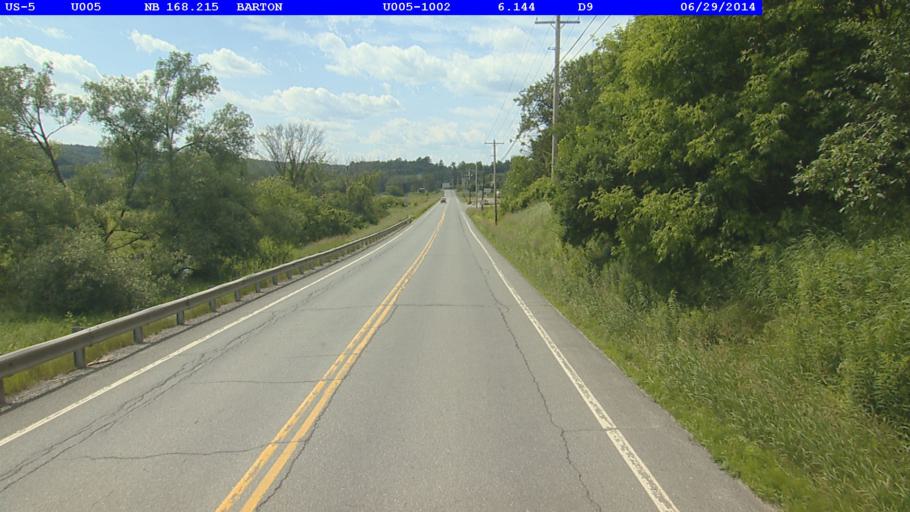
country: US
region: Vermont
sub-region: Orleans County
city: Newport
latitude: 44.7560
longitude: -72.1858
